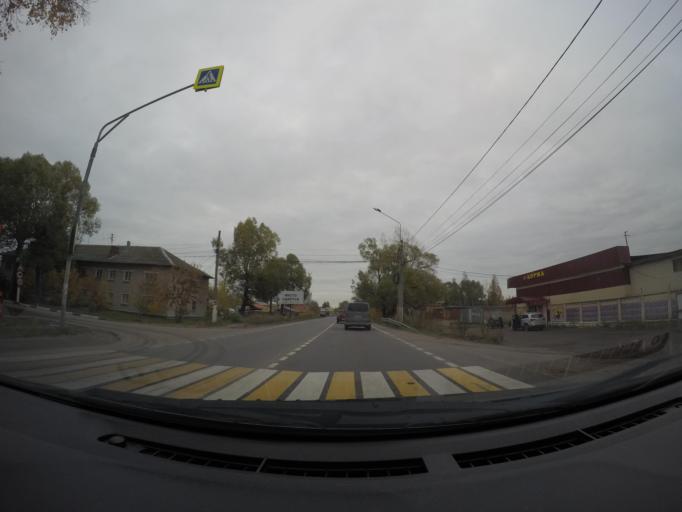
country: RU
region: Moskovskaya
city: Imeni Vorovskogo
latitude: 55.7222
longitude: 38.3351
